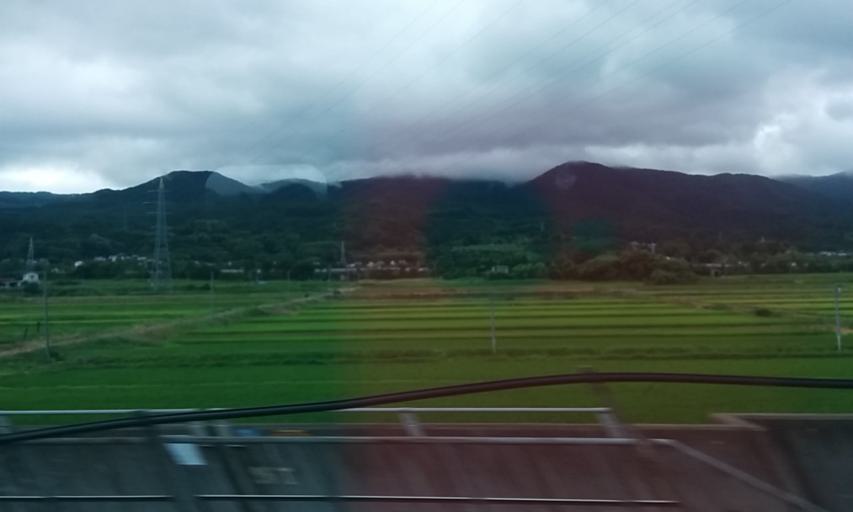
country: JP
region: Fukushima
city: Hobaramachi
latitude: 37.8680
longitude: 140.5271
